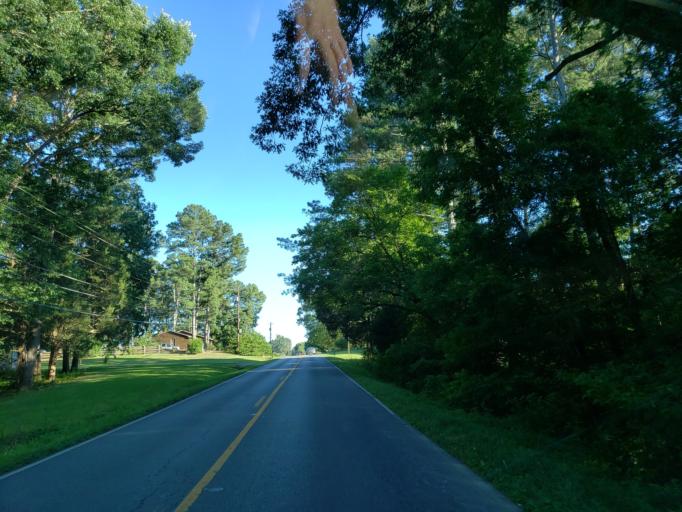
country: US
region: Georgia
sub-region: Polk County
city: Aragon
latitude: 34.0334
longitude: -85.0712
